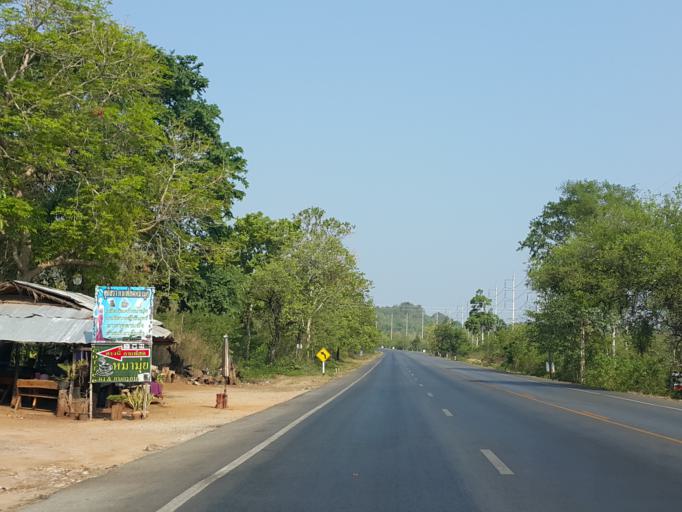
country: TH
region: Kanchanaburi
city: Sai Yok
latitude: 14.1114
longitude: 99.2085
